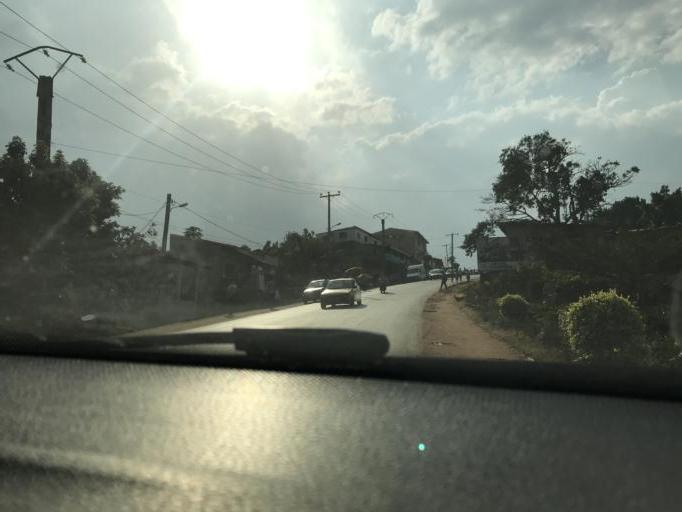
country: CM
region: Centre
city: Yaounde
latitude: 3.8842
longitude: 11.5282
